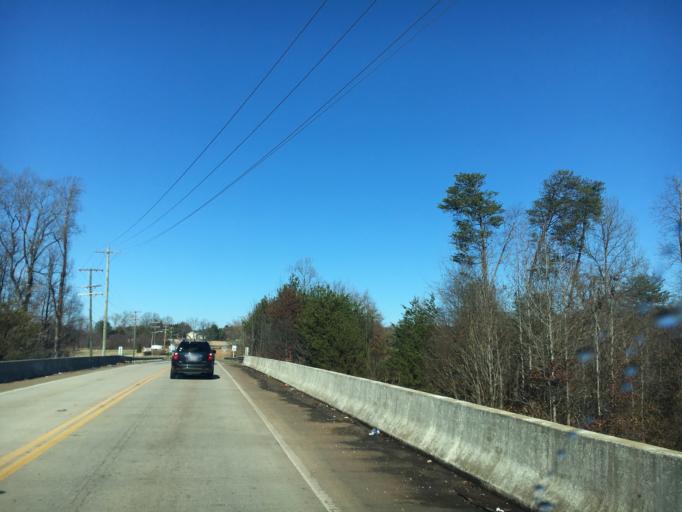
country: US
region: South Carolina
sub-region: Greenville County
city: Taylors
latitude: 34.9172
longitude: -82.2673
